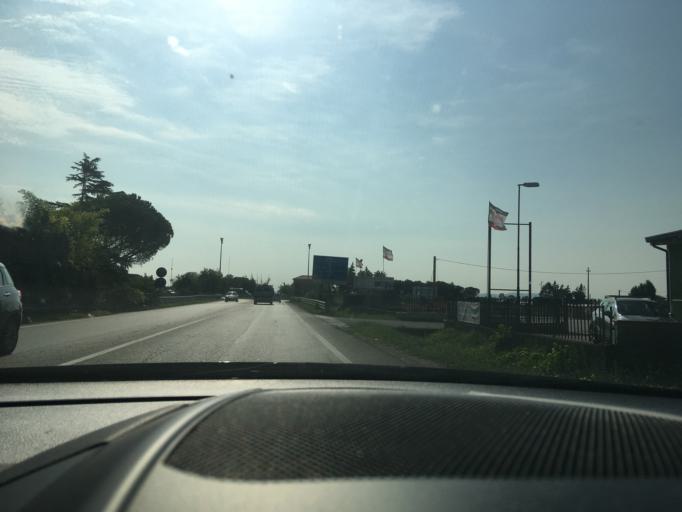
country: IT
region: Emilia-Romagna
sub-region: Provincia di Rimini
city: Santa Giustina
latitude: 44.1042
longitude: 12.4894
